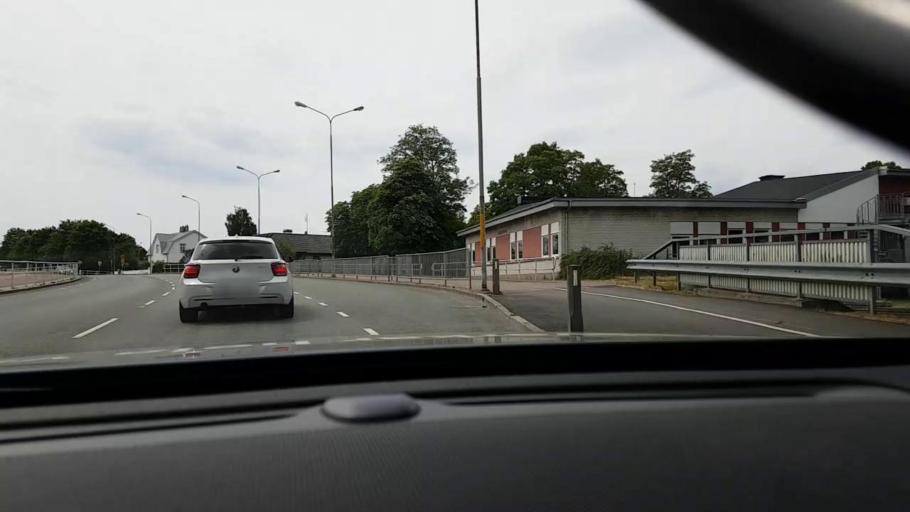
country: SE
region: Skane
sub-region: Hassleholms Kommun
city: Hassleholm
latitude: 56.1646
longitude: 13.7776
